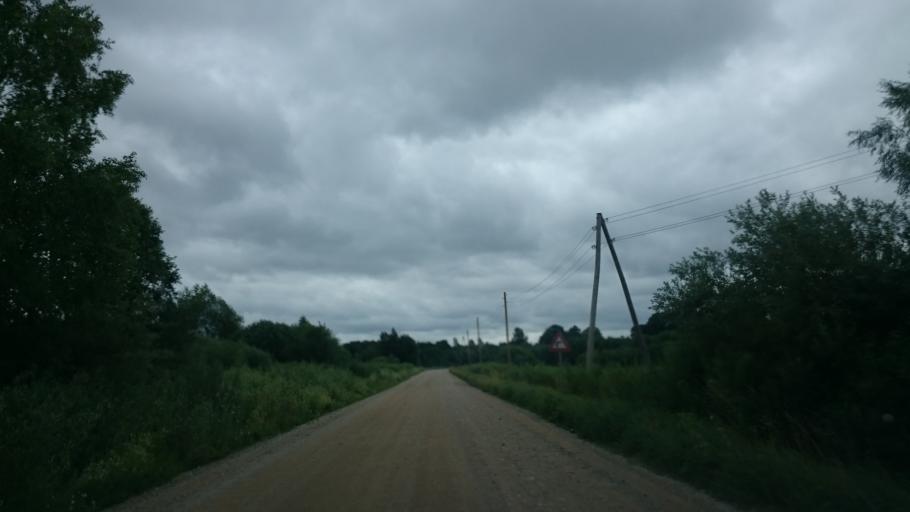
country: LV
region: Durbe
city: Liegi
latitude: 56.7516
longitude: 21.3600
